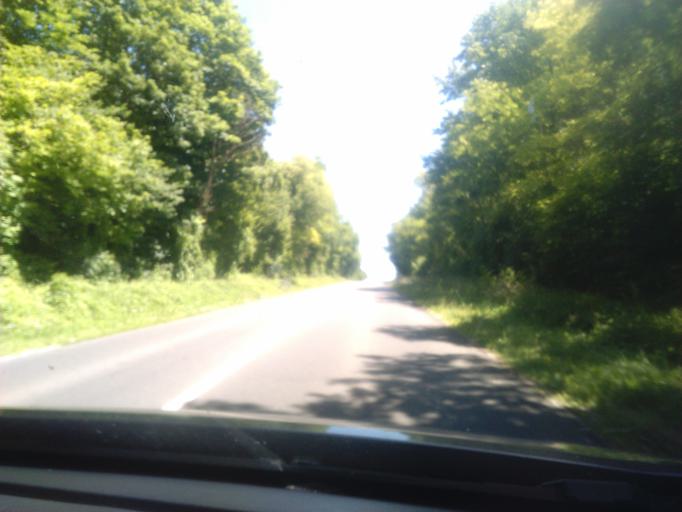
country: FR
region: Centre
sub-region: Departement du Loir-et-Cher
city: Saint-Sulpice-de-Pommeray
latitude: 47.6146
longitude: 1.2281
